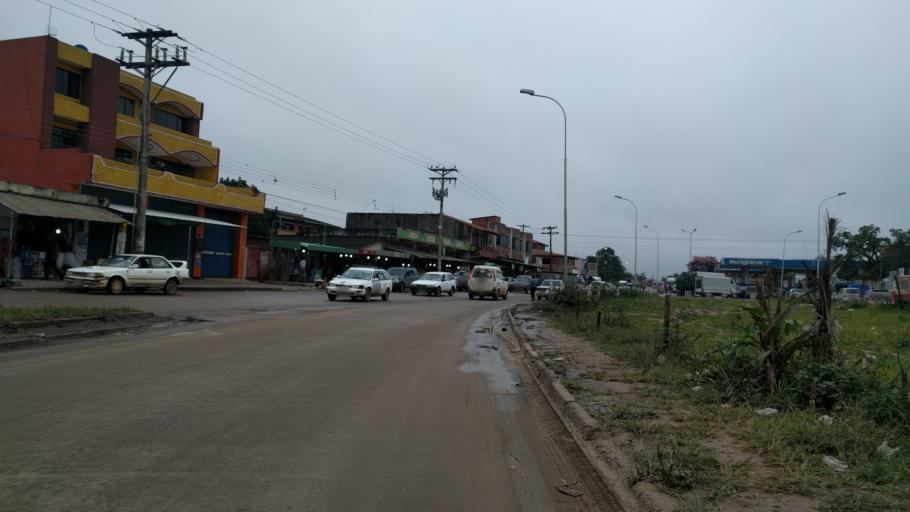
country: BO
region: Santa Cruz
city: Santa Cruz de la Sierra
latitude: -17.8286
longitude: -63.2018
